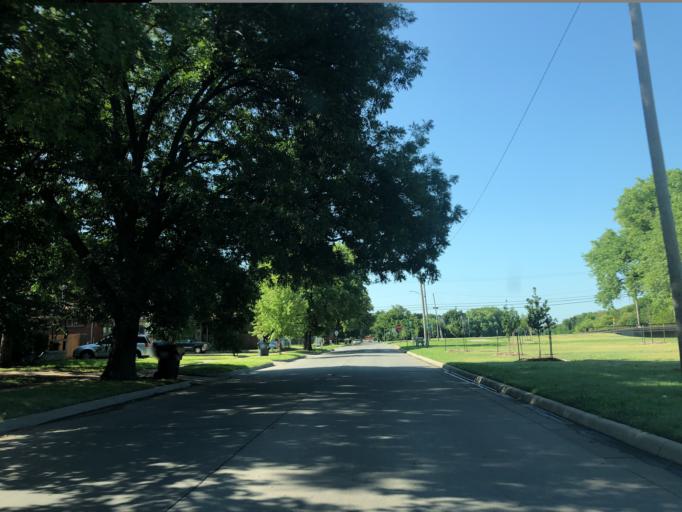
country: US
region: Kansas
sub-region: Sedgwick County
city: Wichita
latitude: 37.7182
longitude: -97.3447
